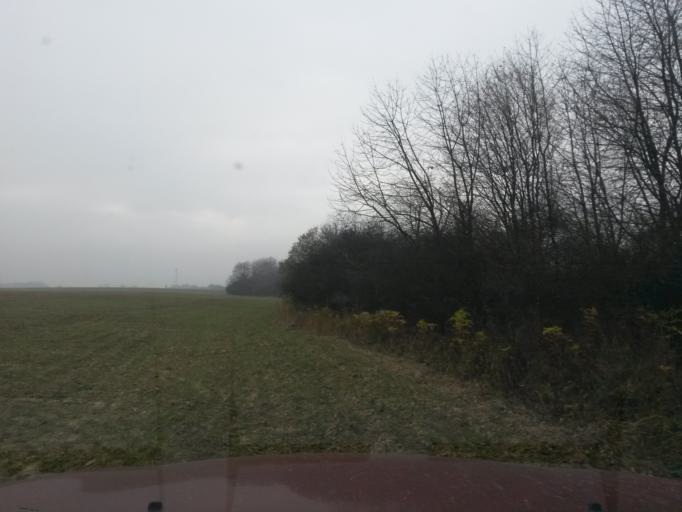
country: SK
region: Presovsky
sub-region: Okres Presov
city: Presov
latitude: 48.8952
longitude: 21.2789
